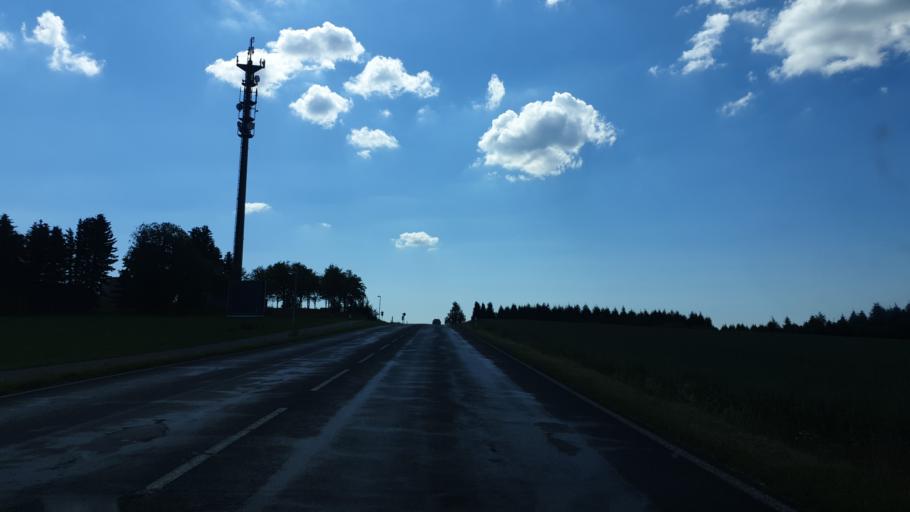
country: DE
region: Saxony
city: Marienberg
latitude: 50.6620
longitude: 13.1464
